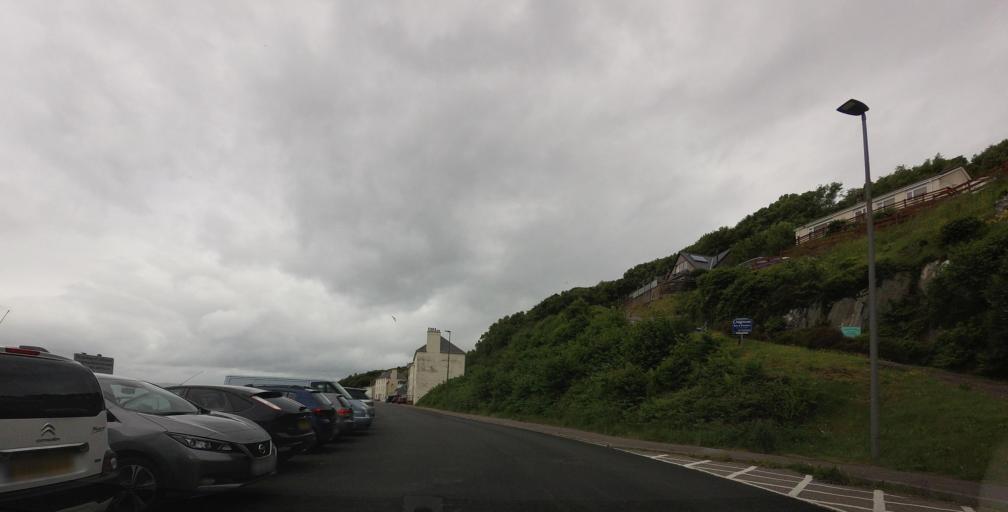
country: GB
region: Scotland
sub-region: Highland
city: Portree
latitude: 57.0047
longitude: -5.8224
